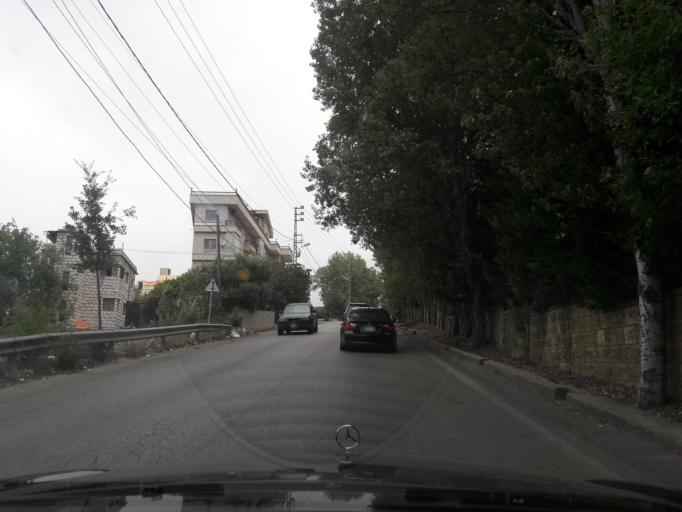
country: LB
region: Mont-Liban
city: Djounie
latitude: 33.9138
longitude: 35.6912
